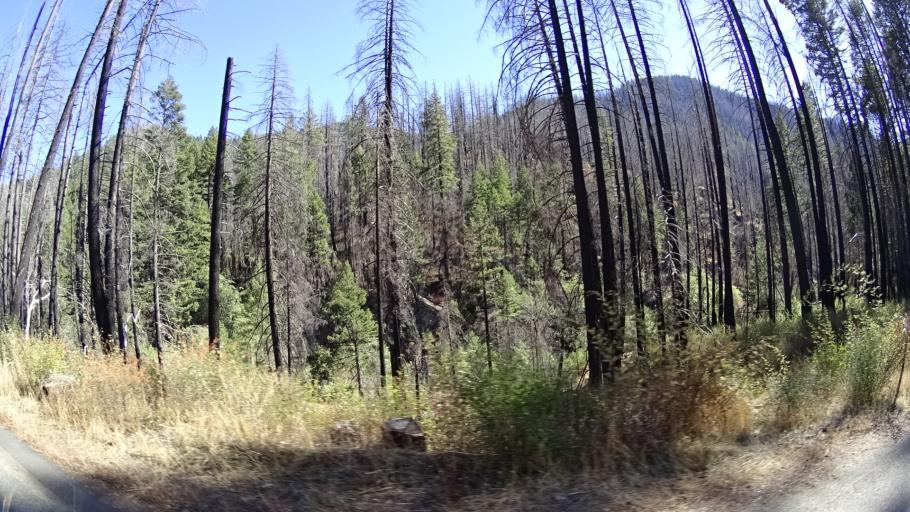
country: US
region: California
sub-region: Siskiyou County
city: Happy Camp
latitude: 41.3038
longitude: -123.0744
